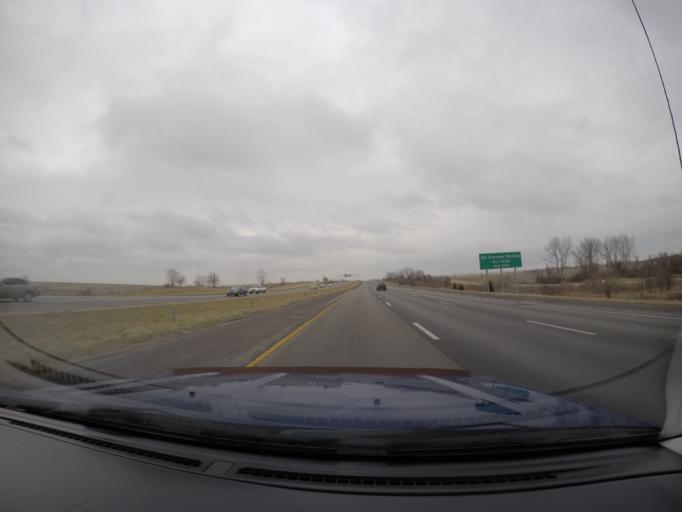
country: US
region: Missouri
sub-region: Platte County
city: Platte City
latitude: 39.3376
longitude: -94.7286
